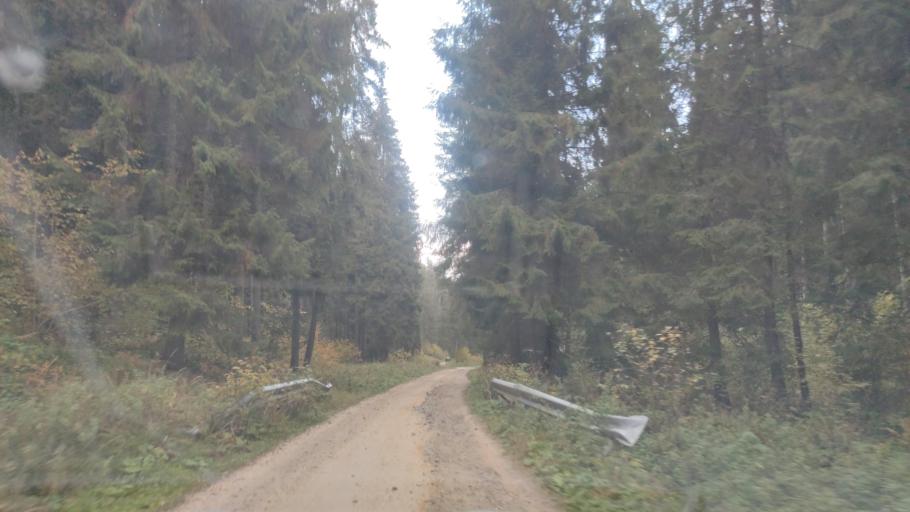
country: RO
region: Harghita
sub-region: Comuna Madaras
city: Madaras
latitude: 46.4761
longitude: 25.6491
